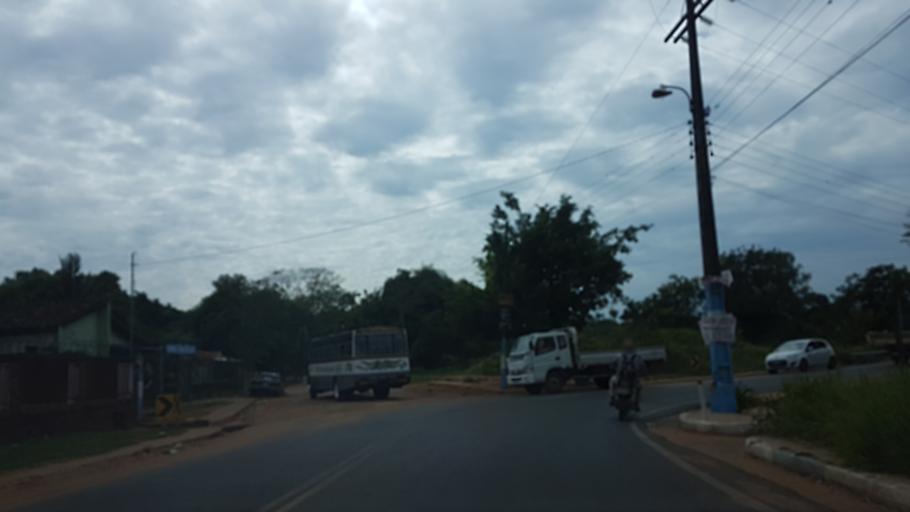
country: PY
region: Central
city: Capiata
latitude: -25.3014
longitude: -57.4649
